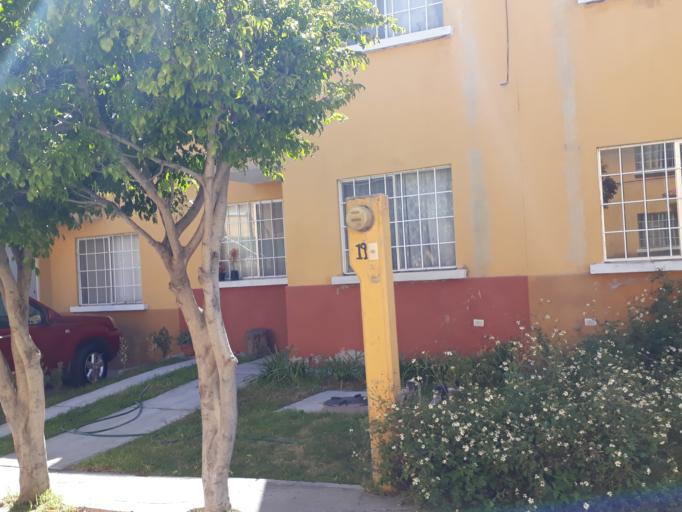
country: MX
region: Aguascalientes
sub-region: Aguascalientes
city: Aguascalientes
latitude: 21.8771
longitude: -102.2421
